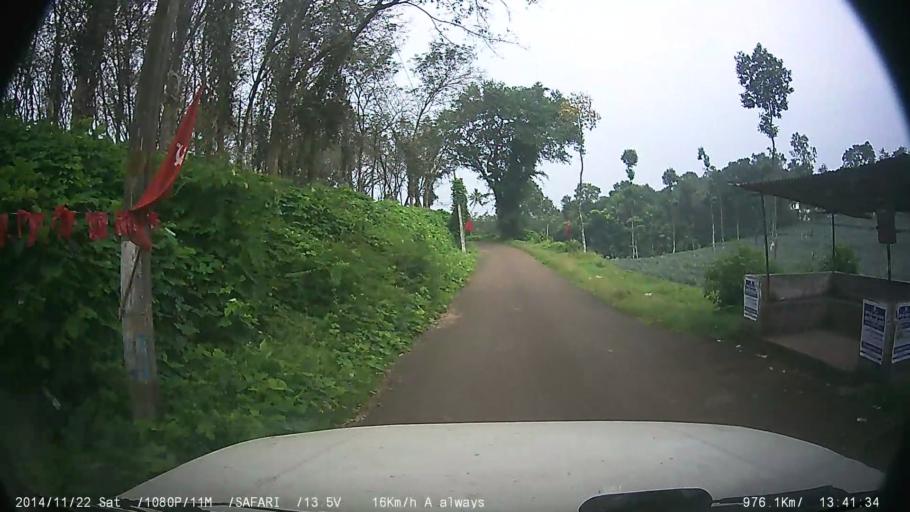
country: IN
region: Kerala
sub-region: Kottayam
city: Palackattumala
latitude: 9.7846
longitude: 76.5628
